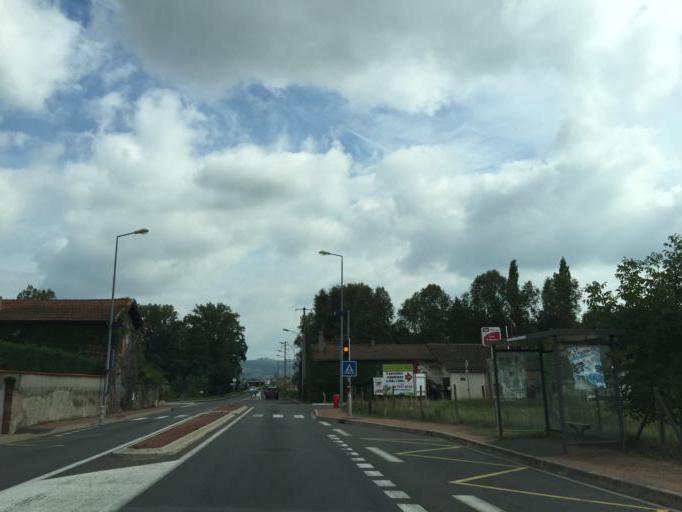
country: FR
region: Rhone-Alpes
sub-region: Departement de la Loire
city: Bonson
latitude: 45.5182
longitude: 4.2237
